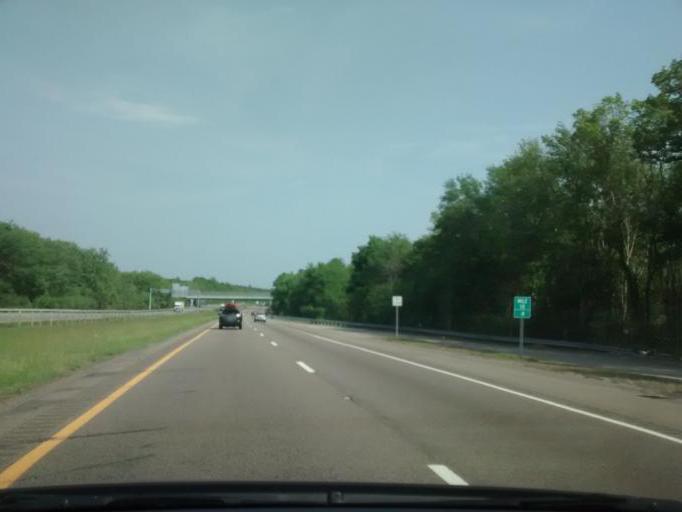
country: US
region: Massachusetts
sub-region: Plymouth County
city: Middleborough Center
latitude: 41.8707
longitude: -70.8934
